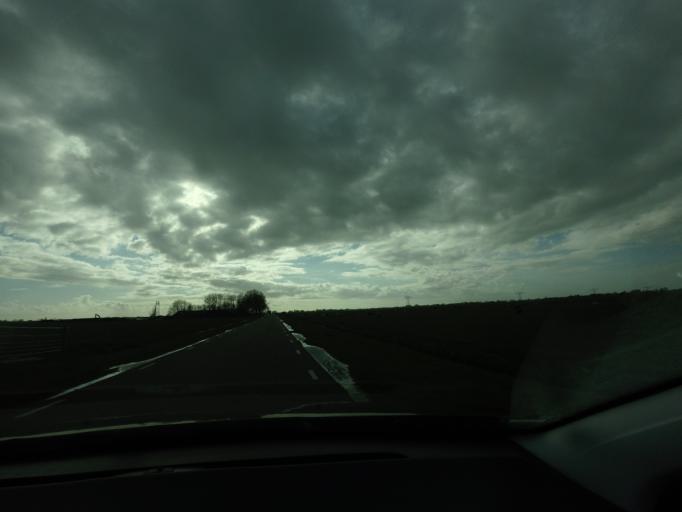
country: NL
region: Friesland
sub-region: Gemeente Boarnsterhim
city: Jirnsum
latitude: 53.0773
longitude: 5.7808
